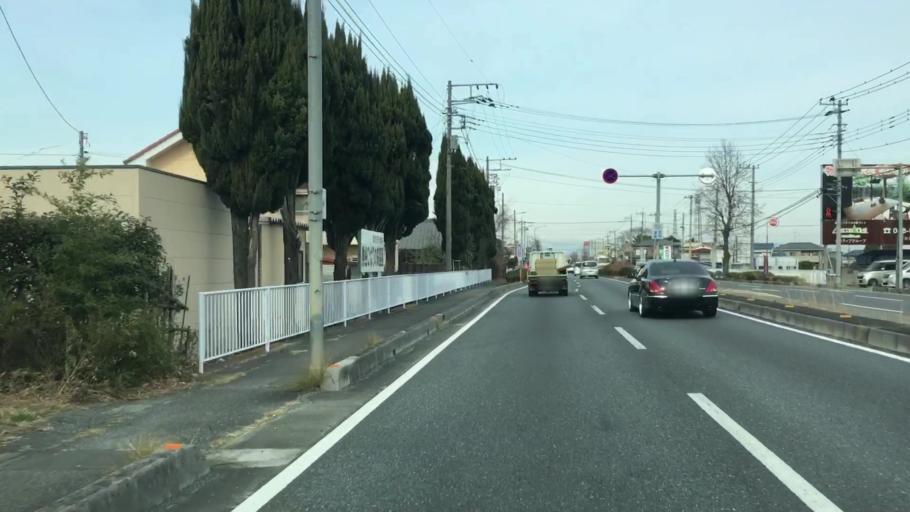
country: JP
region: Saitama
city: Kumagaya
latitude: 36.1625
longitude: 139.3707
